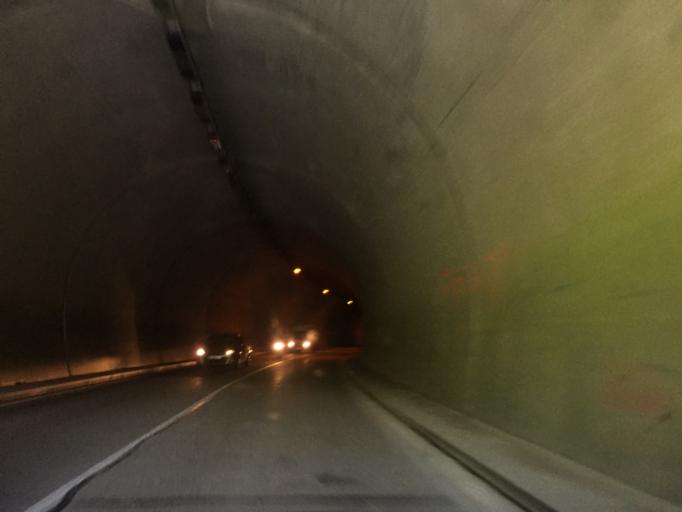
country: FR
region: Rhone-Alpes
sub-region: Departement de l'Isere
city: Saint-Laurent-du-Pont
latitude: 45.3777
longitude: 5.7476
